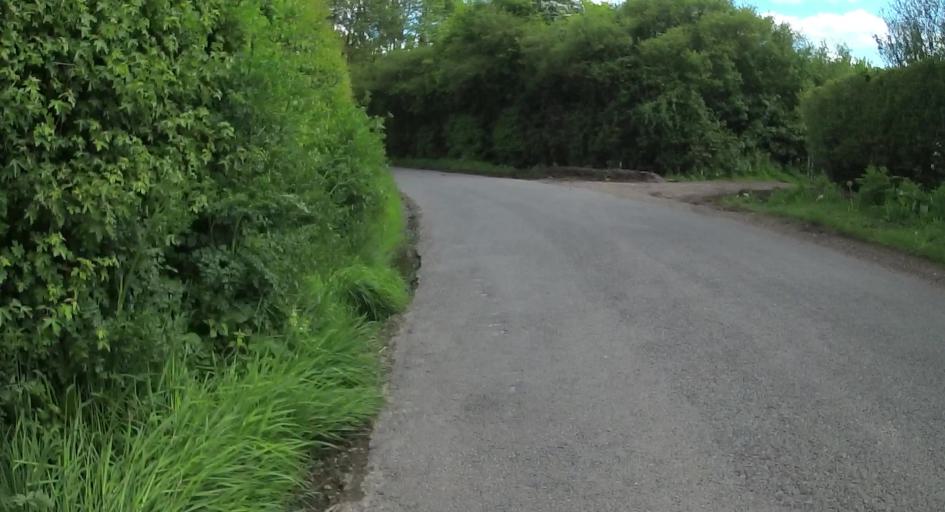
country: GB
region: England
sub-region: West Berkshire
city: Stratfield Mortimer
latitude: 51.3377
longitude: -1.0377
